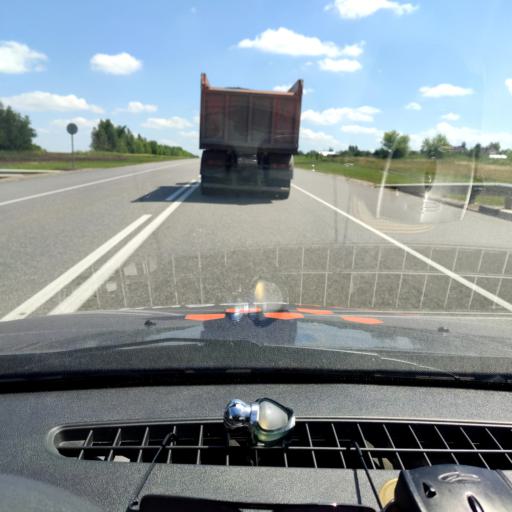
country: RU
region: Orjol
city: Zmiyevka
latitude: 52.8354
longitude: 36.2658
